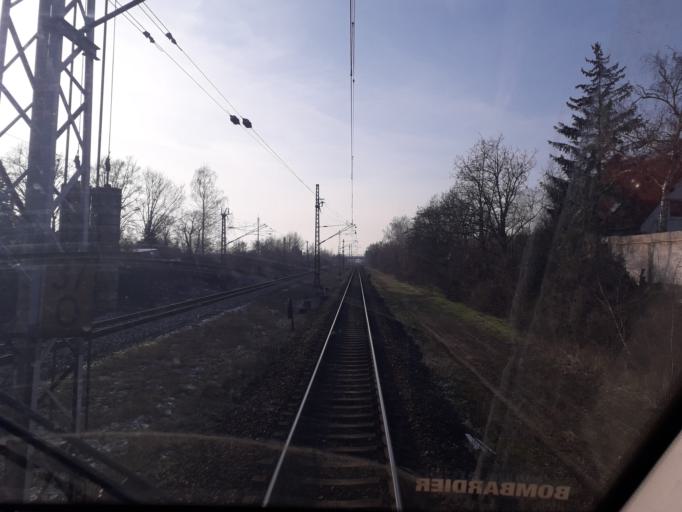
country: DE
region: Berlin
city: Altglienicke
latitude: 52.3993
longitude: 13.5295
